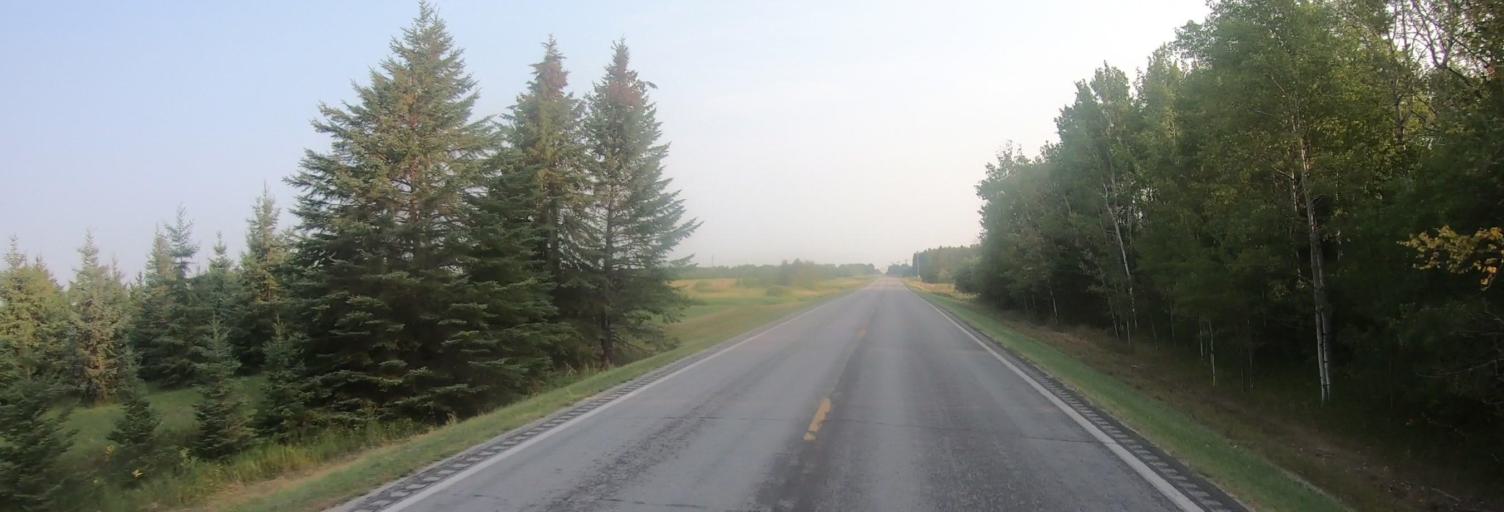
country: US
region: Minnesota
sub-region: Roseau County
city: Warroad
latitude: 48.7819
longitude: -95.3305
